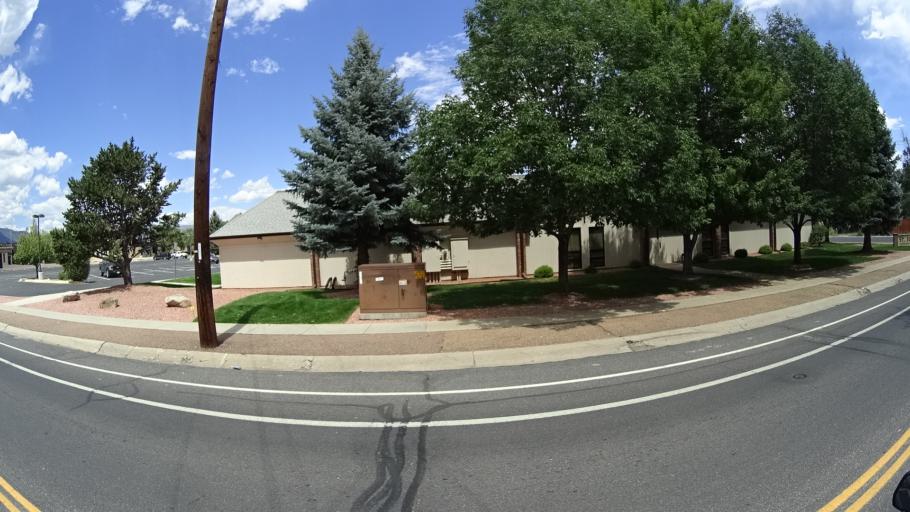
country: US
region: Colorado
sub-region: El Paso County
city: Colorado Springs
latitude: 38.8070
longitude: -104.8183
